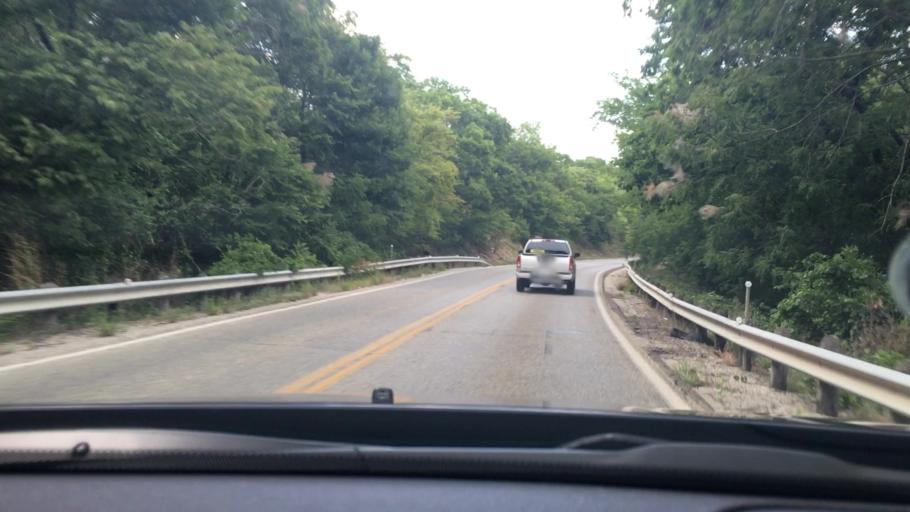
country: US
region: Oklahoma
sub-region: Pontotoc County
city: Ada
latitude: 34.5672
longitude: -96.6338
